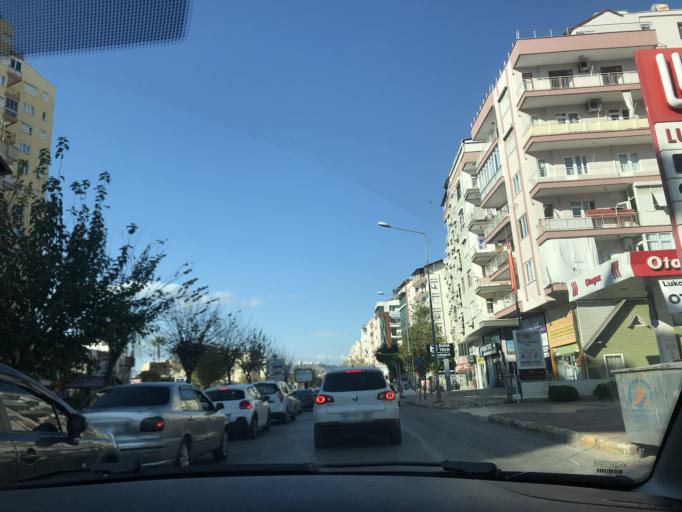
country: TR
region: Antalya
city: Antalya
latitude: 36.9062
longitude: 30.7000
